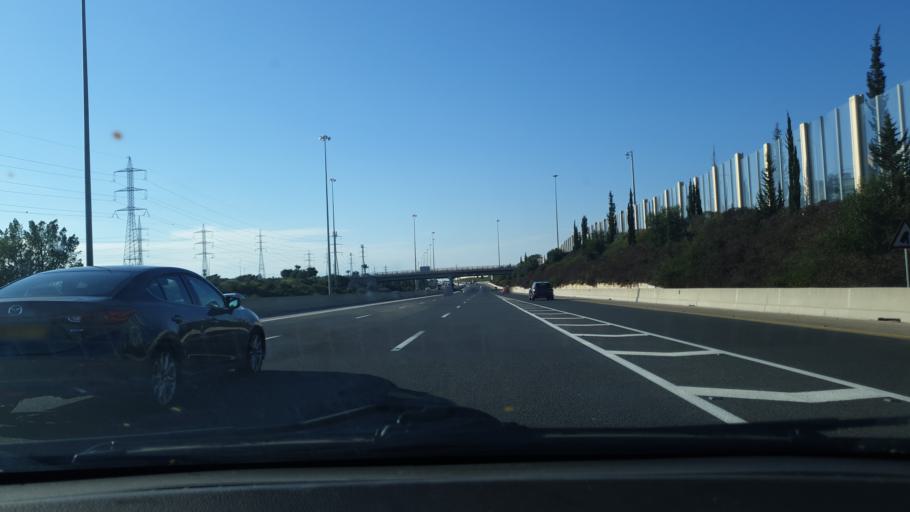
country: IL
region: Central District
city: Rishon LeZiyyon
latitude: 31.9614
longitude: 34.7706
